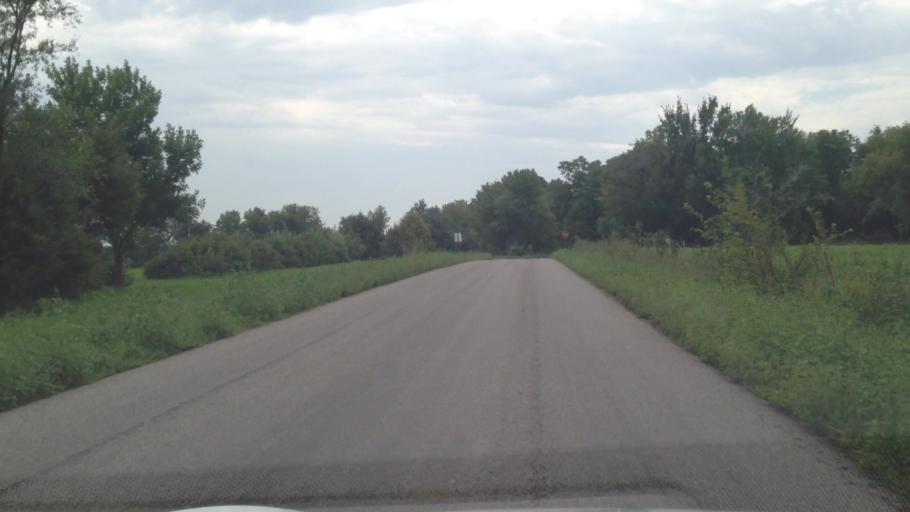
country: US
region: Kansas
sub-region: Crawford County
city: Girard
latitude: 37.5005
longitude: -94.8699
